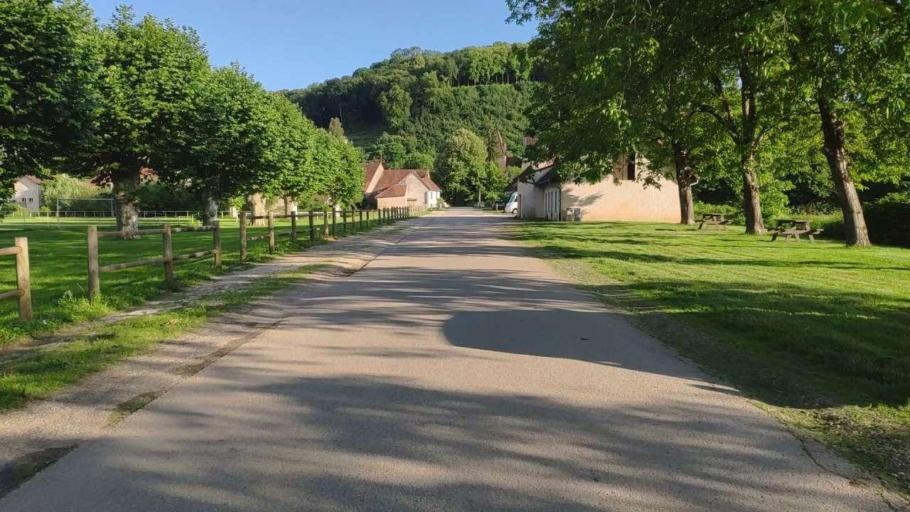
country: FR
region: Franche-Comte
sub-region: Departement du Jura
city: Bletterans
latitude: 46.7624
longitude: 5.5354
